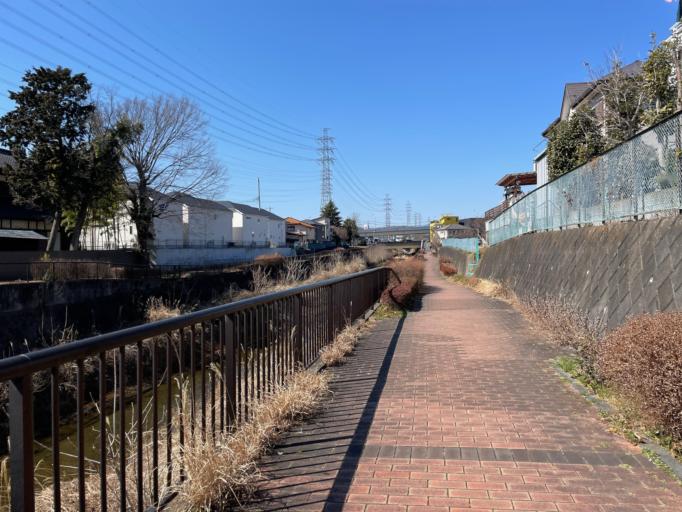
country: JP
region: Tokyo
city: Hachioji
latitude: 35.6788
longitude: 139.3569
